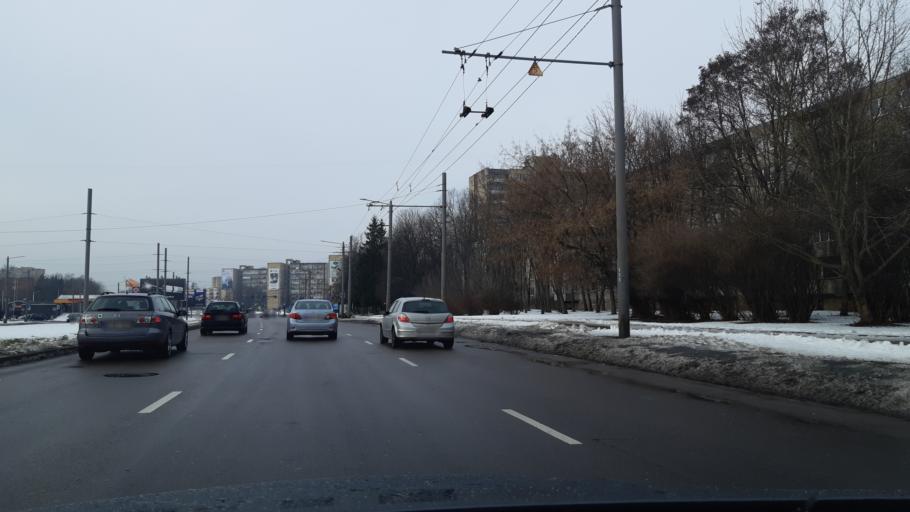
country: LT
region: Kauno apskritis
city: Dainava (Kaunas)
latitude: 54.9123
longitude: 23.9603
